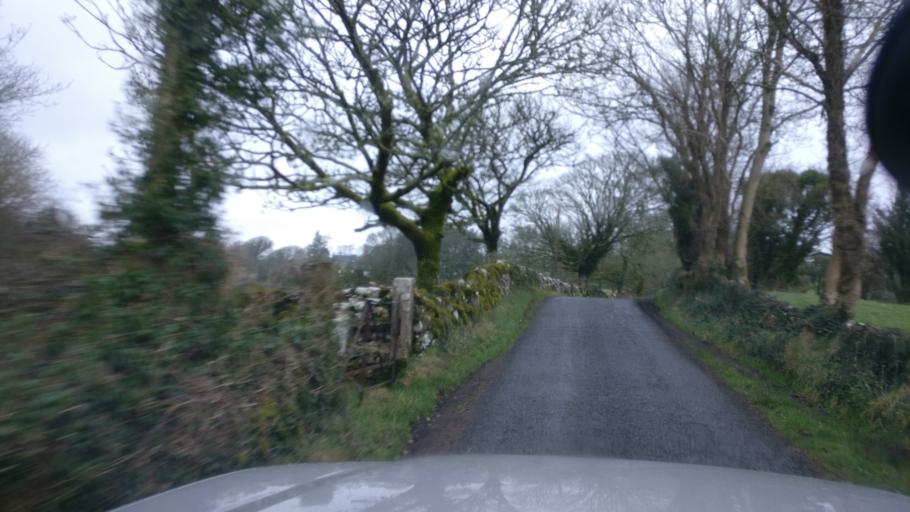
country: IE
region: Connaught
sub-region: County Galway
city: Loughrea
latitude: 53.1788
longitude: -8.6083
